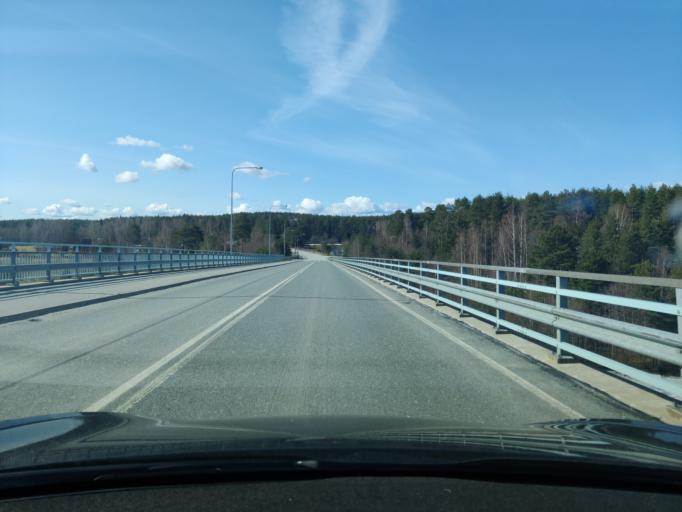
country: FI
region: Northern Savo
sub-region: Kuopio
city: Vehmersalmi
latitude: 62.7687
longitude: 28.0016
